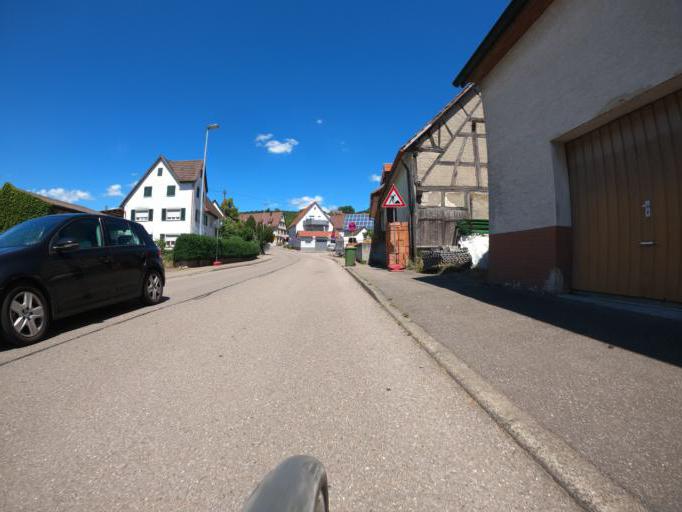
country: DE
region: Baden-Wuerttemberg
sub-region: Regierungsbezirk Stuttgart
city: Sersheim
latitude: 48.9982
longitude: 9.0218
